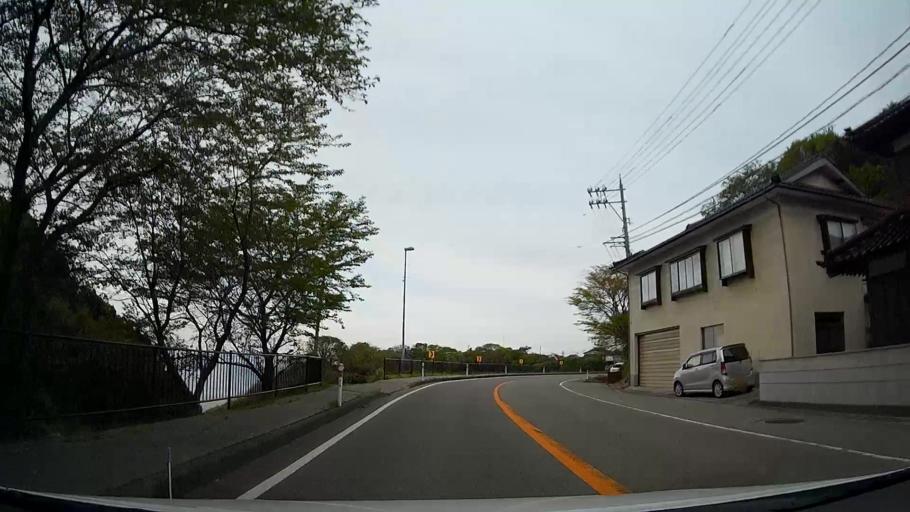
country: JP
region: Ishikawa
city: Nanao
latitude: 37.3971
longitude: 136.9367
